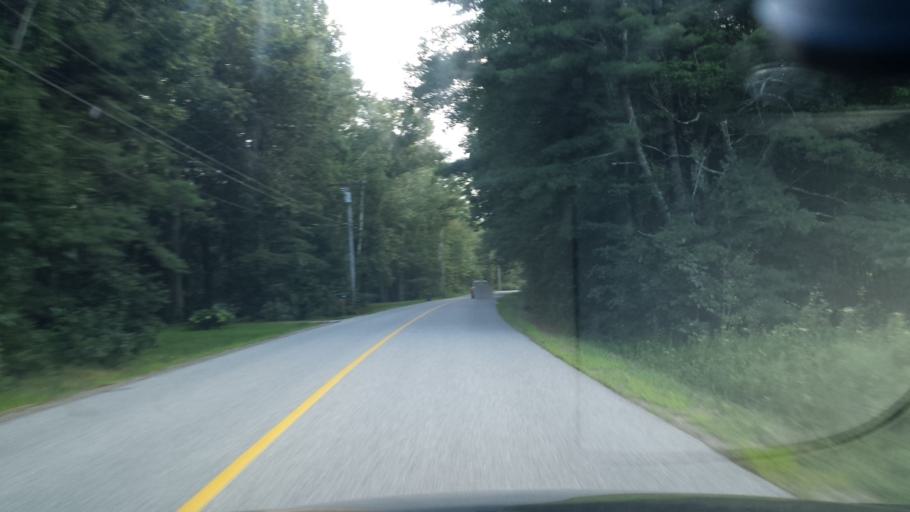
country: US
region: Maine
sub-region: York County
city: Biddeford
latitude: 43.4365
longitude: -70.4475
